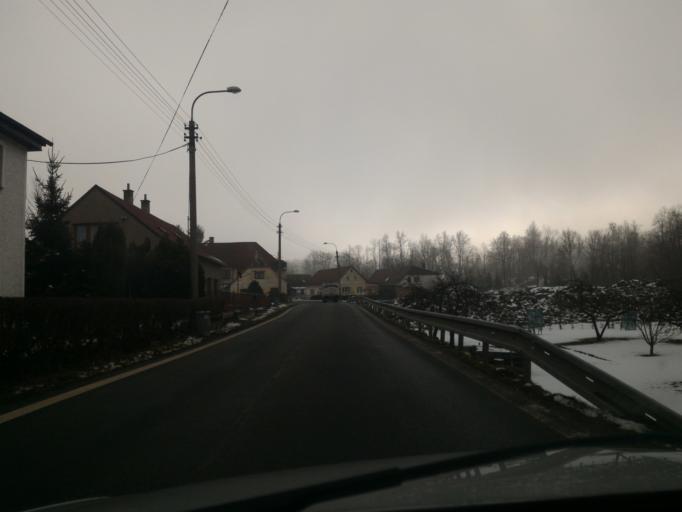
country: CZ
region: Liberecky
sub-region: Okres Liberec
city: Hejnice
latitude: 50.8752
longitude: 15.1993
